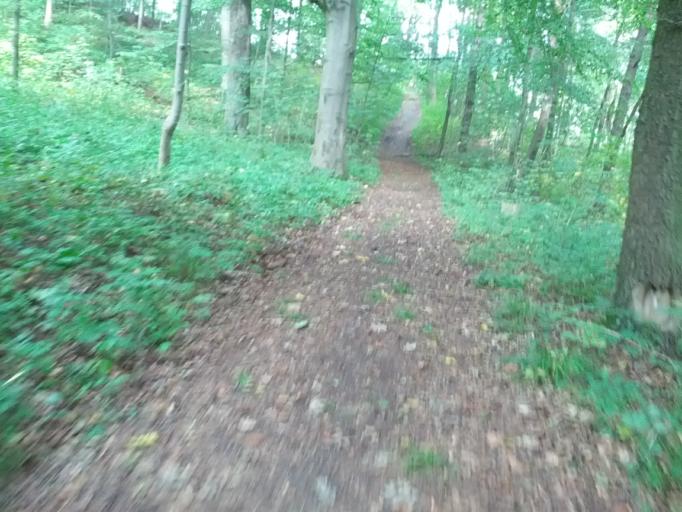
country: DE
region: Thuringia
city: Eisenach
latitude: 50.9899
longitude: 10.2847
